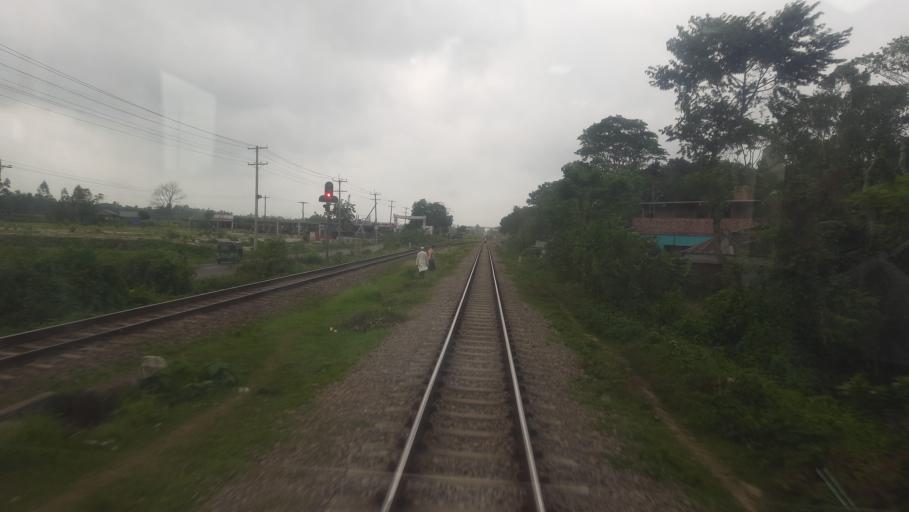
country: BD
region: Dhaka
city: Narsingdi
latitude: 23.9567
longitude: 90.8033
